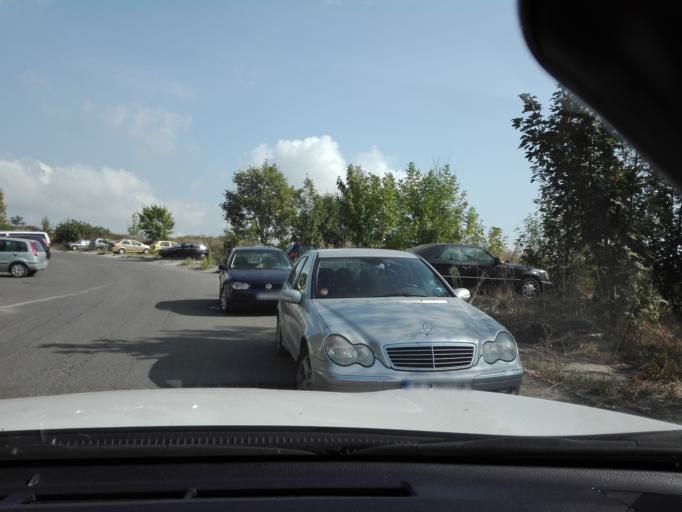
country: BG
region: Burgas
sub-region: Obshtina Burgas
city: Burgas
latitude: 42.4517
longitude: 27.4251
